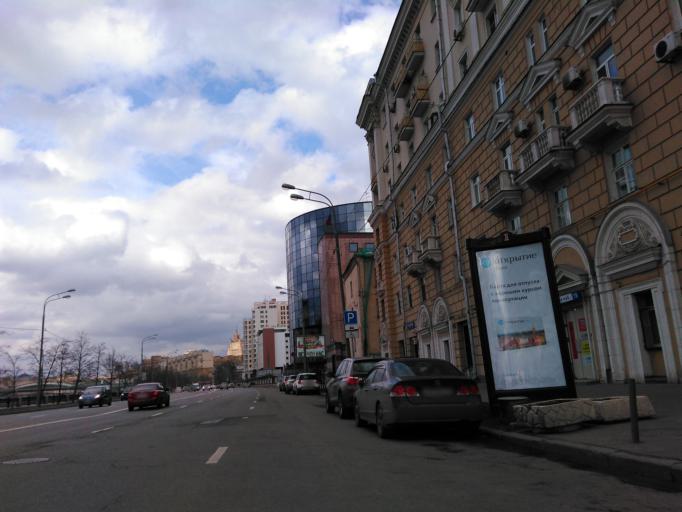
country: RU
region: Moskovskaya
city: Dorogomilovo
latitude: 55.7343
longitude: 37.5645
